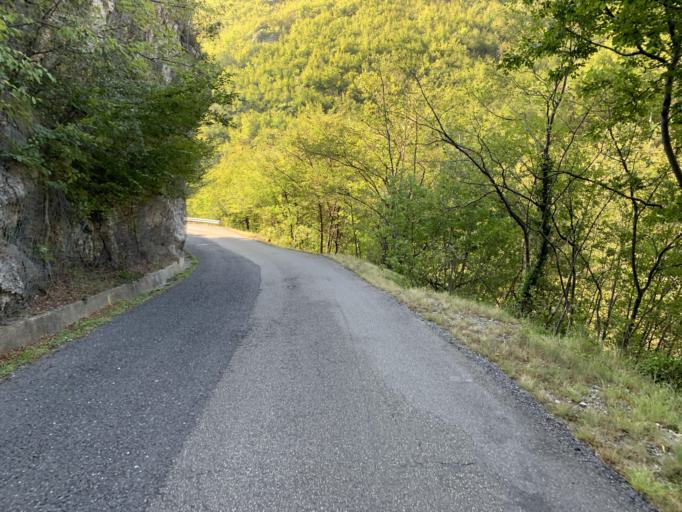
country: IT
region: Liguria
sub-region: Provincia di Savona
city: Magliolo
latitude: 44.1997
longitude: 8.2264
